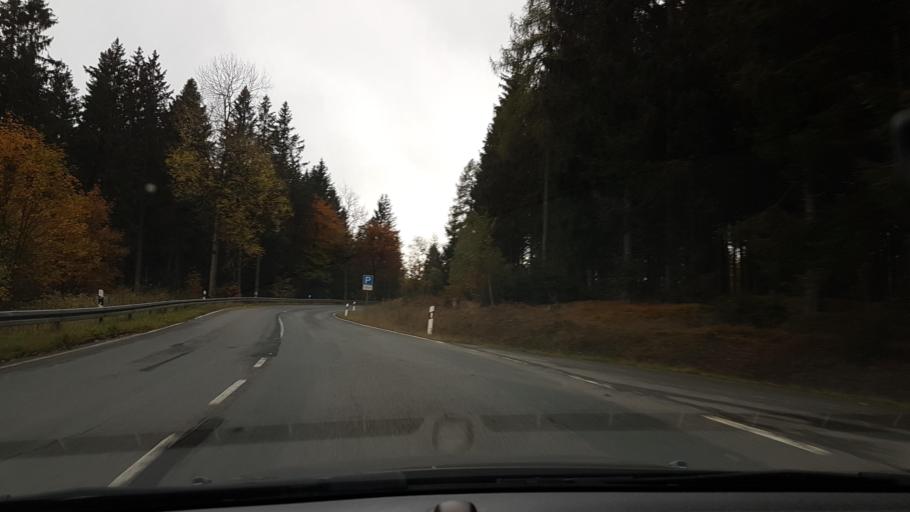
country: DE
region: Lower Saxony
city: Wildemann
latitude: 51.8093
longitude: 10.2712
